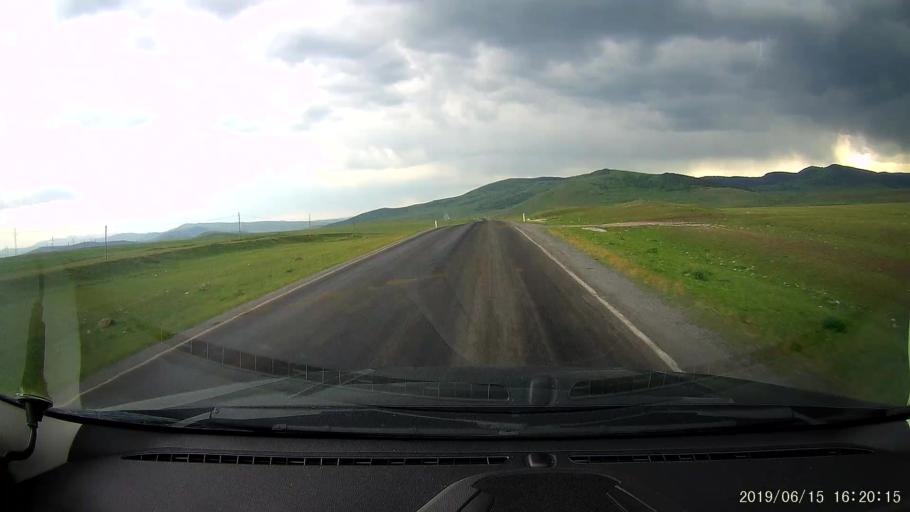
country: TR
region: Ardahan
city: Hanak
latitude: 41.2175
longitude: 42.8484
